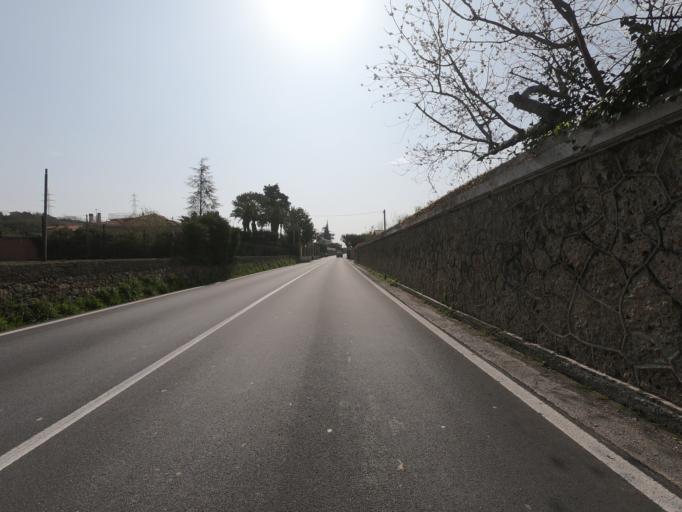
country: IT
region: Liguria
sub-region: Provincia di Savona
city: Cisano
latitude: 44.0850
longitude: 8.1502
